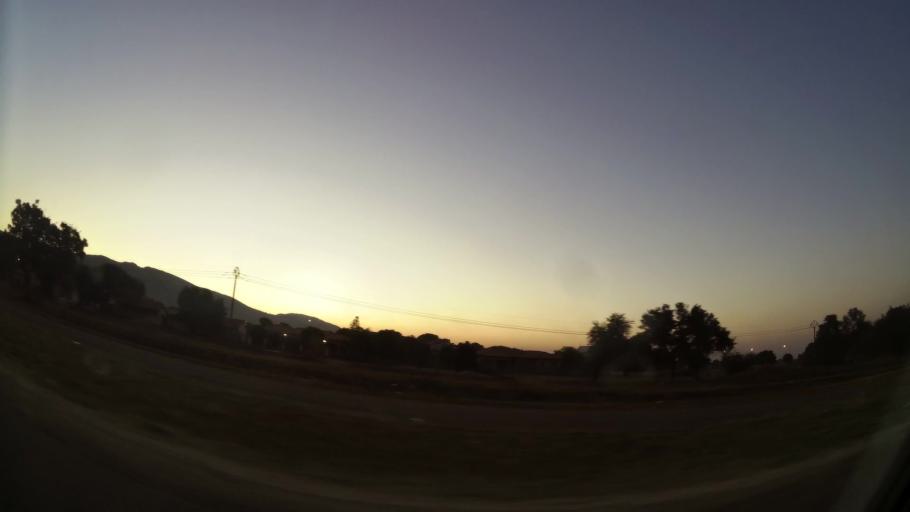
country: ZA
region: North-West
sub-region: Bojanala Platinum District Municipality
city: Rustenburg
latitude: -25.6556
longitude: 27.2187
